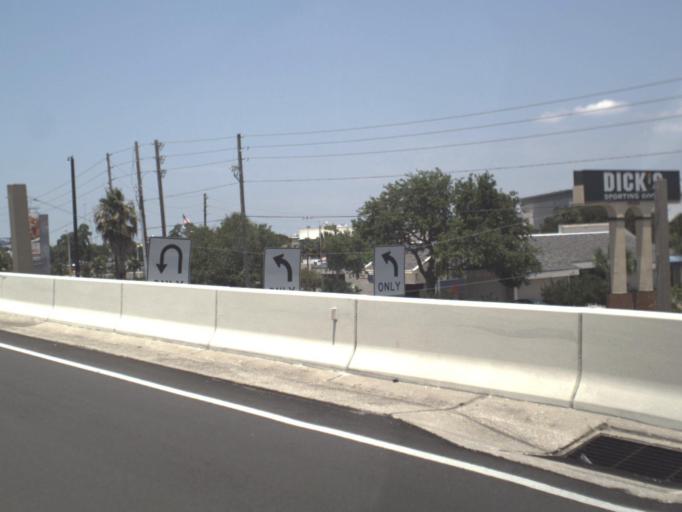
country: US
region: Florida
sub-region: Pinellas County
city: Dunedin
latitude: 28.0135
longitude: -82.7354
